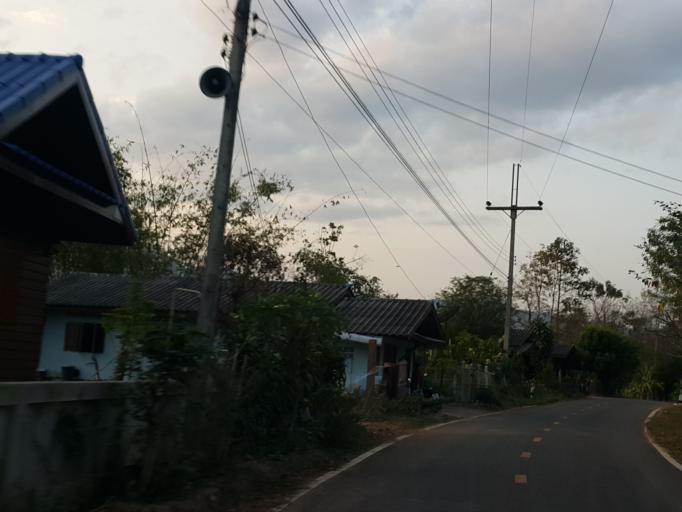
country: TH
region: Lampang
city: Mueang Pan
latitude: 18.7902
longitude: 99.4925
